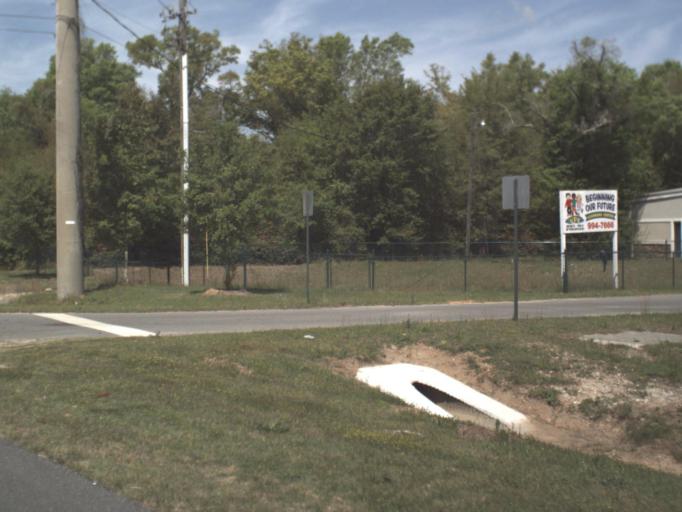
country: US
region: Florida
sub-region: Santa Rosa County
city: Milton
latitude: 30.6029
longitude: -87.0910
